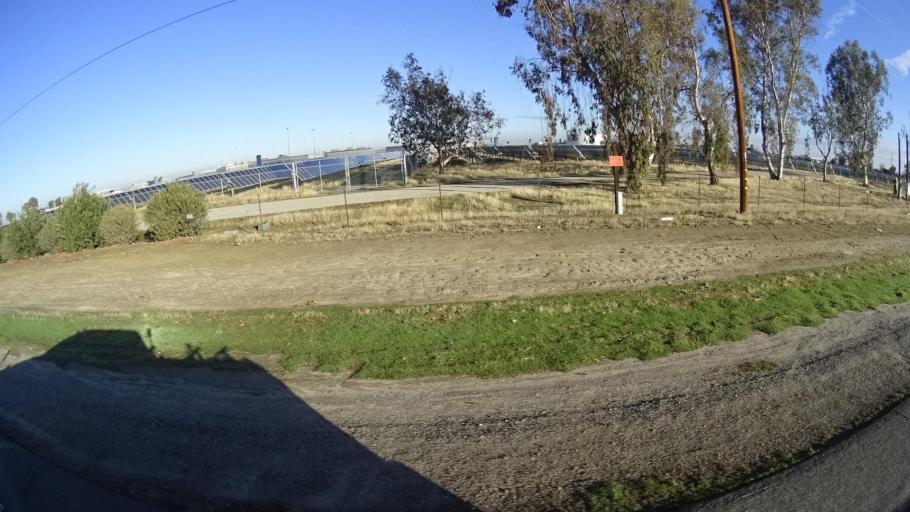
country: US
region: California
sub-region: Kern County
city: Delano
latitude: 35.7759
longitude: -119.3078
